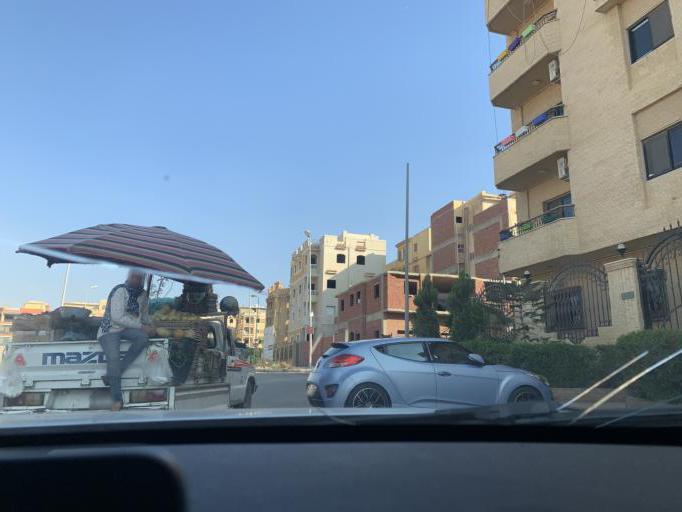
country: EG
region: Muhafazat al Qalyubiyah
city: Al Khankah
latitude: 30.0020
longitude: 31.4830
